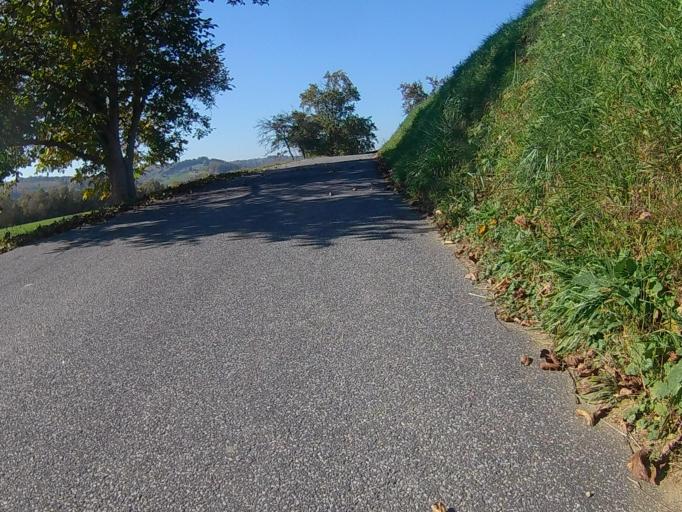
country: SI
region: Sveti Jurij v Slovenskih Goricah
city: Jurovski Dol
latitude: 46.5768
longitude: 15.7448
